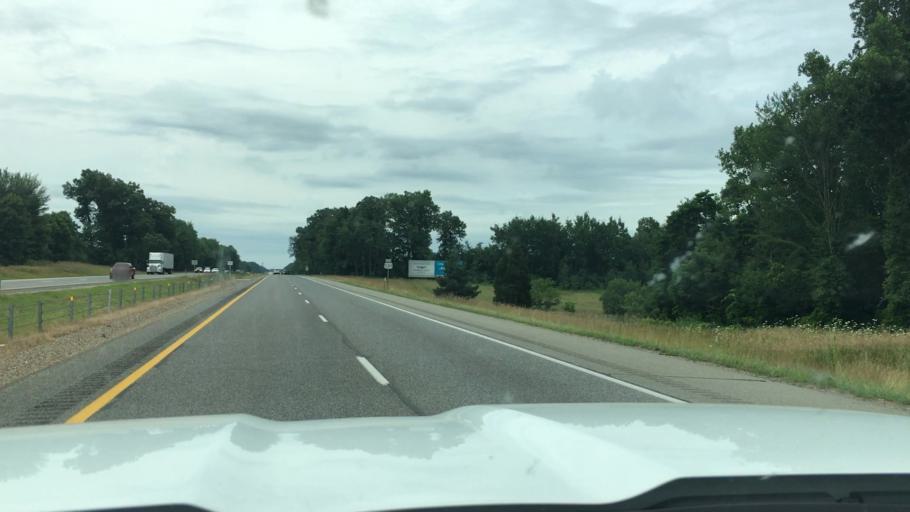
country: US
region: Michigan
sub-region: Allegan County
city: Otsego
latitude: 42.5320
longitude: -85.6591
